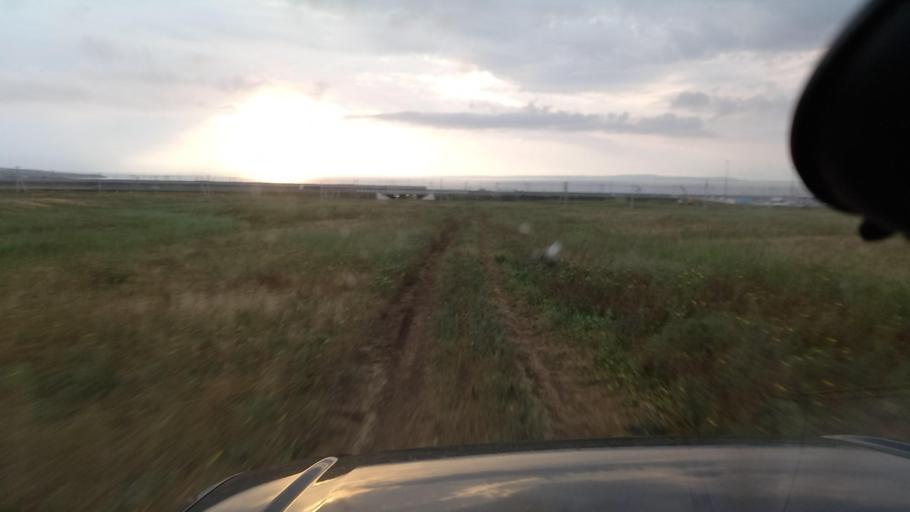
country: RU
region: Krasnodarskiy
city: Taman'
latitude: 45.2123
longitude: 36.7677
